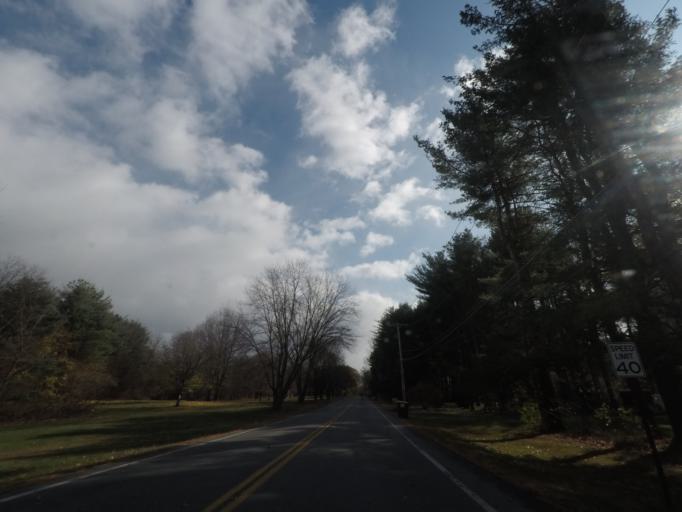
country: US
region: New York
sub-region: Saratoga County
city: Country Knolls
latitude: 42.8978
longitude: -73.8182
